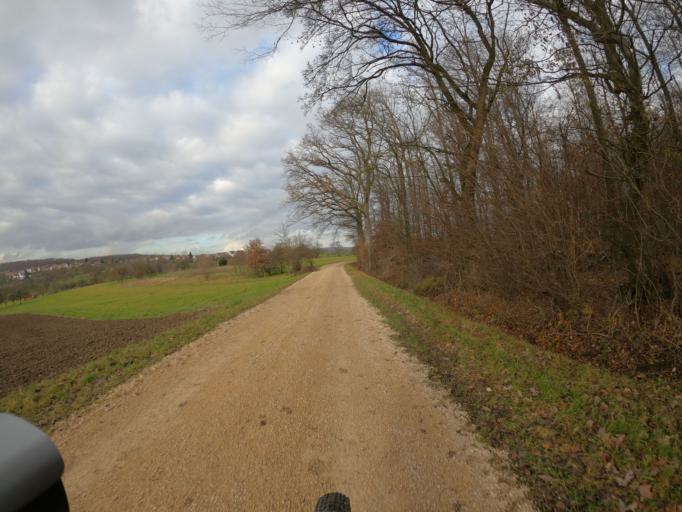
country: DE
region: Baden-Wuerttemberg
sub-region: Regierungsbezirk Stuttgart
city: Notzingen
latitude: 48.6691
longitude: 9.4778
